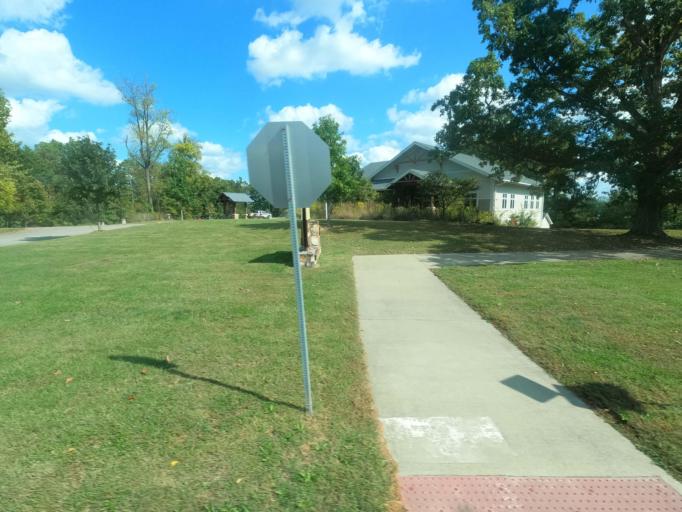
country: US
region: Illinois
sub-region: Johnson County
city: Vienna
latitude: 37.4210
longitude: -88.8931
